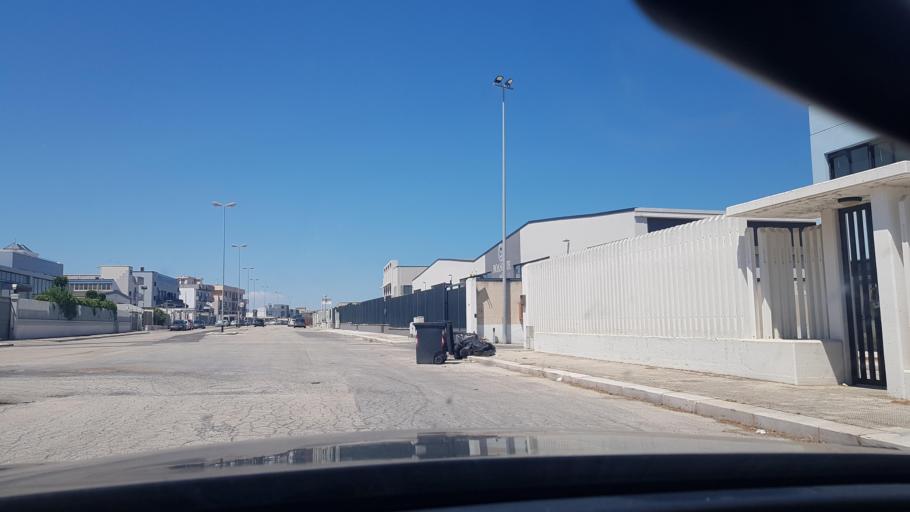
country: IT
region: Apulia
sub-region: Provincia di Barletta - Andria - Trani
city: Barletta
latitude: 41.3046
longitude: 16.3267
